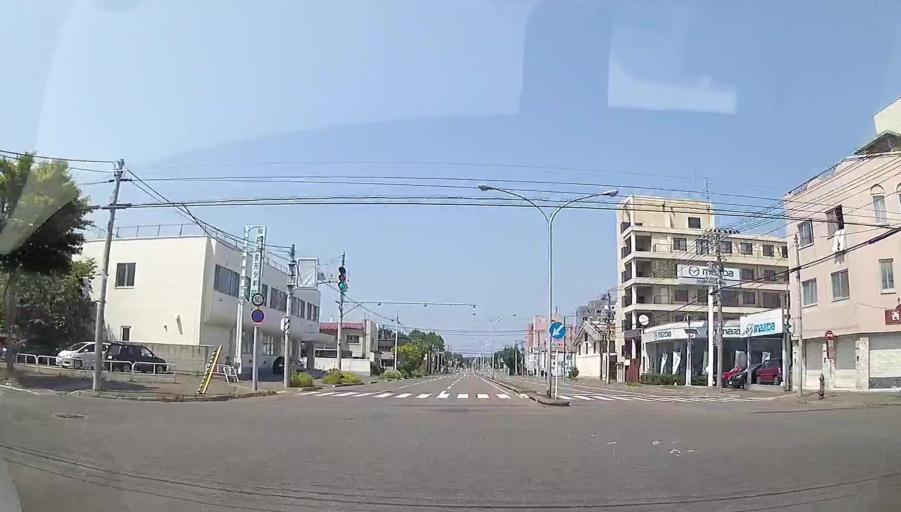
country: JP
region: Hokkaido
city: Obihiro
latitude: 42.9258
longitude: 143.1999
